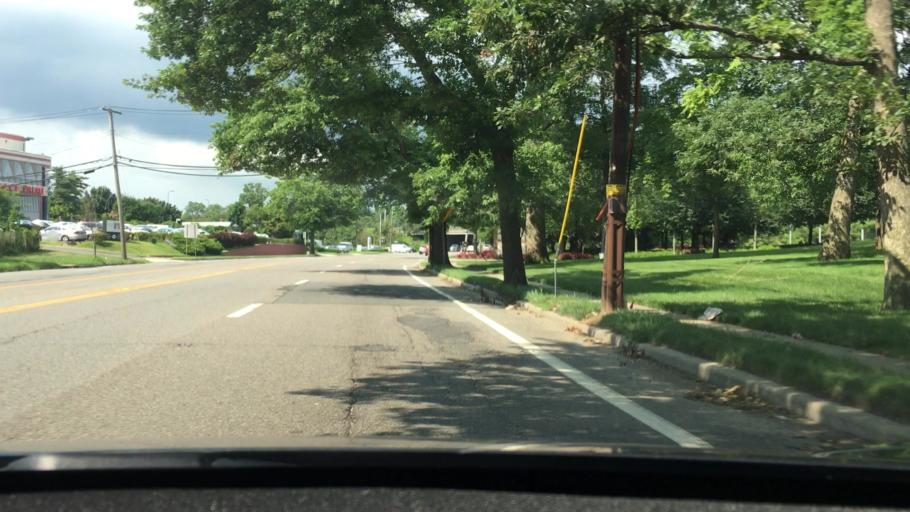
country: US
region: New York
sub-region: Nassau County
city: Old Bethpage
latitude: 40.7829
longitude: -73.4451
